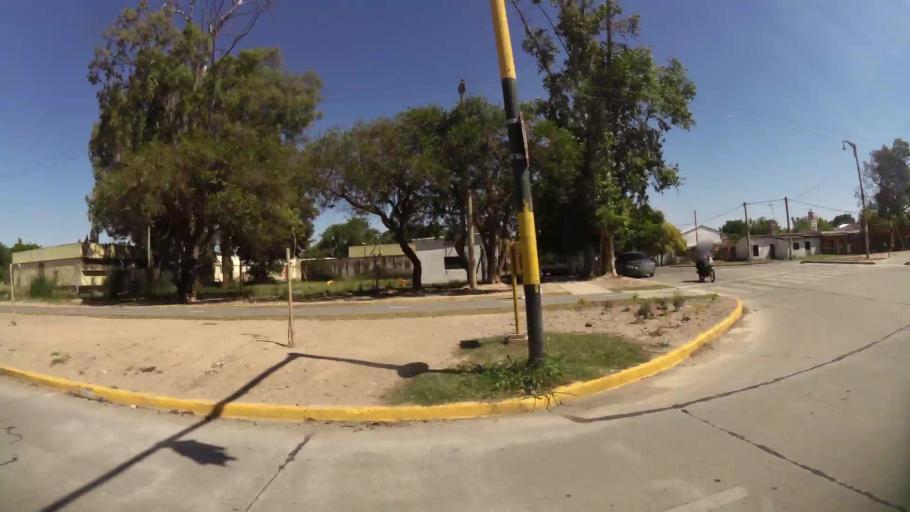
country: AR
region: Cordoba
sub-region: Departamento de Capital
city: Cordoba
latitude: -31.3796
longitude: -64.1449
